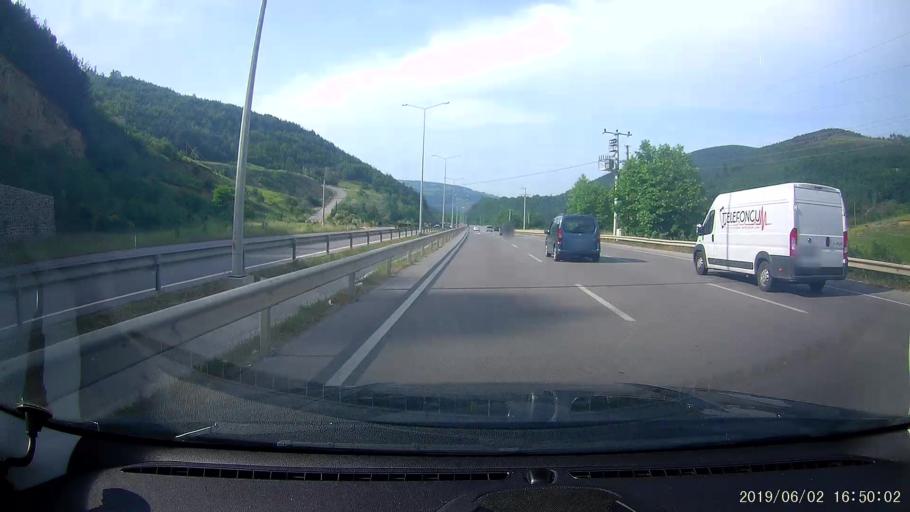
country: TR
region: Samsun
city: Samsun
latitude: 41.2464
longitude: 36.1726
